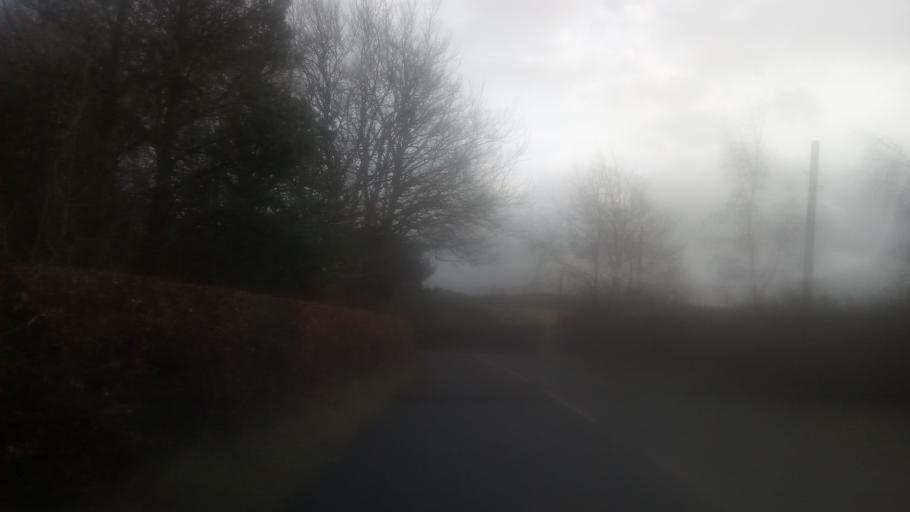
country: GB
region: Scotland
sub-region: The Scottish Borders
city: Jedburgh
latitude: 55.4768
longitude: -2.5359
